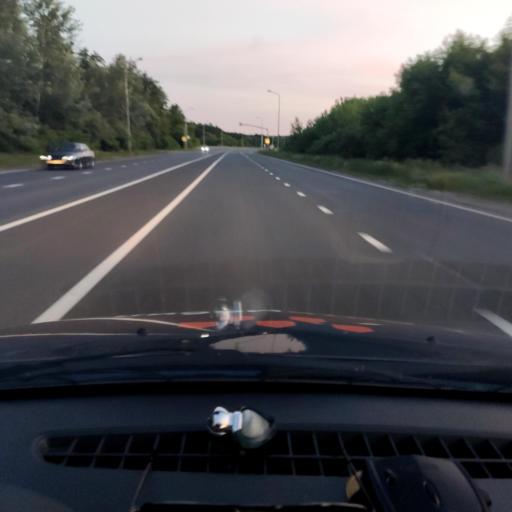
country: RU
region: Belgorod
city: Staryy Oskol
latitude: 51.3501
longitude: 37.8271
